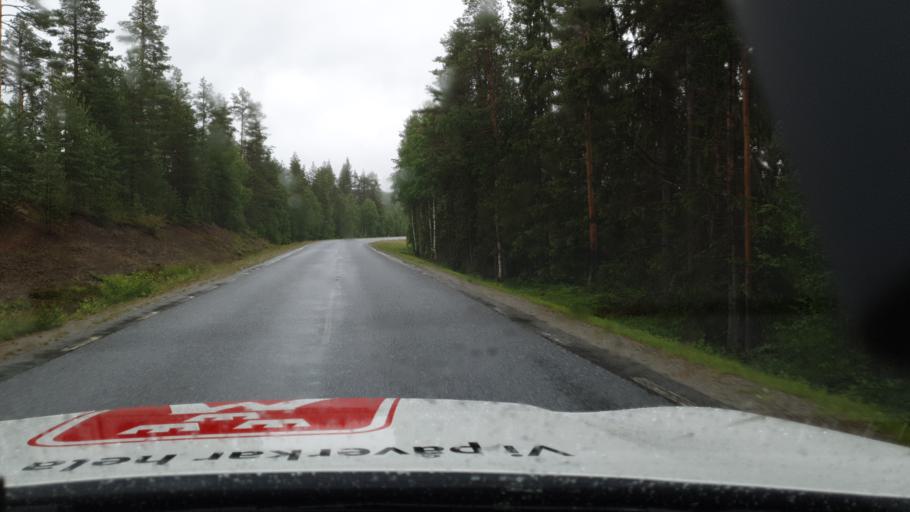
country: SE
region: Vaesterbotten
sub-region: Asele Kommun
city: Asele
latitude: 64.2468
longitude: 17.2837
